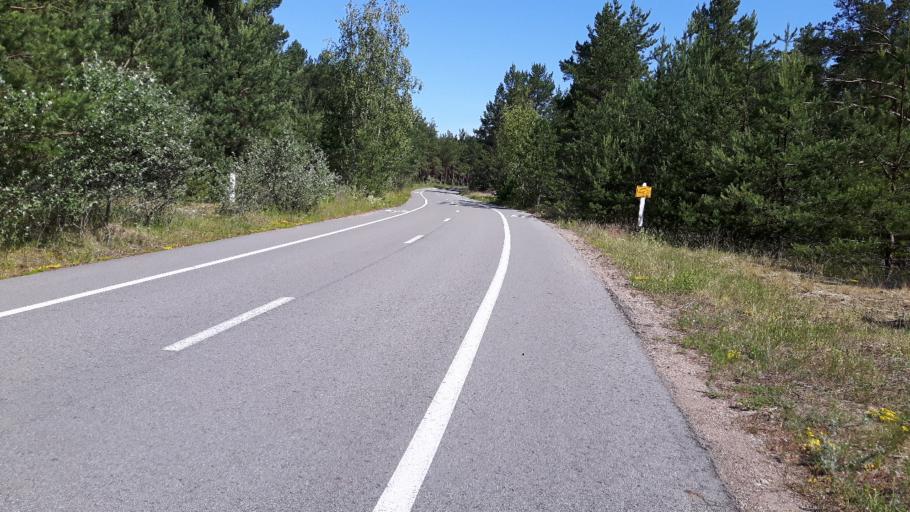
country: LT
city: Nida
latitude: 55.3250
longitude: 21.0266
